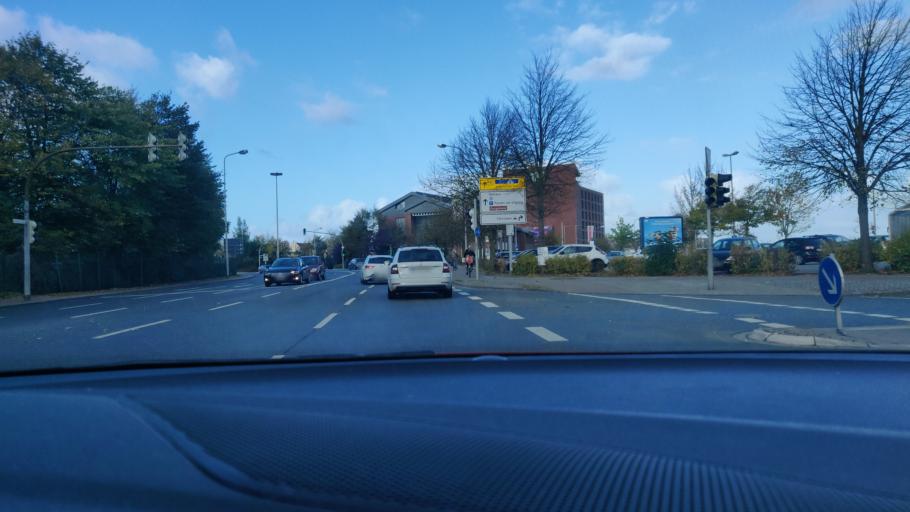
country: DE
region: Lower Saxony
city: Cuxhaven
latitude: 53.8623
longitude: 8.7023
